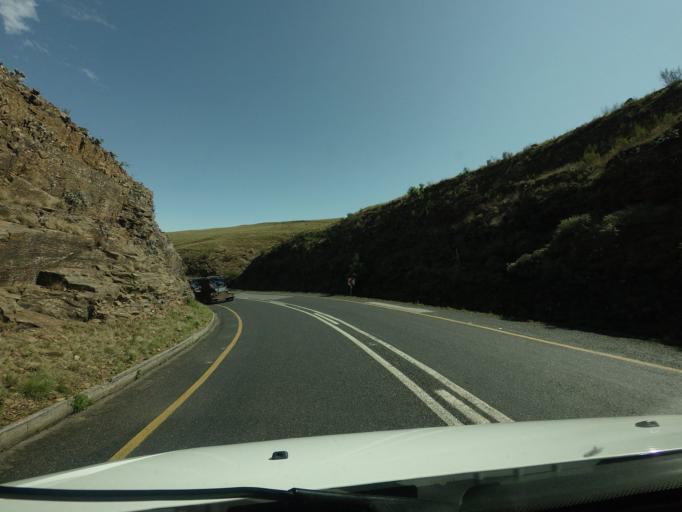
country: ZA
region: Mpumalanga
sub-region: Ehlanzeni District
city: Lydenburg
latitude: -25.1556
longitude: 30.6246
